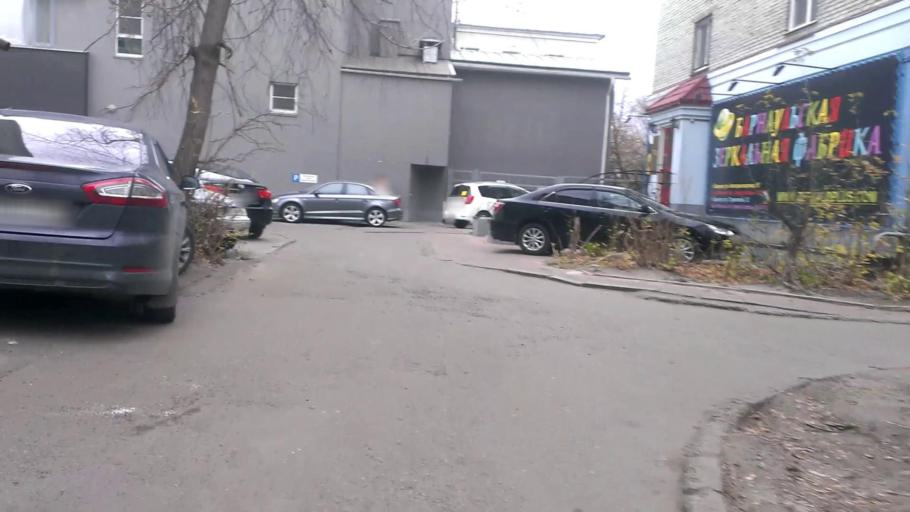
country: RU
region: Altai Krai
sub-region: Gorod Barnaulskiy
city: Barnaul
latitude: 53.3528
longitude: 83.7650
